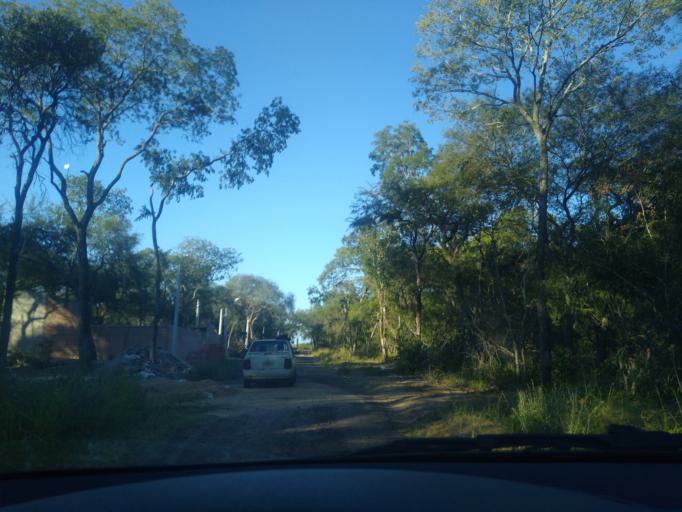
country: AR
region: Chaco
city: Resistencia
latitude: -27.4111
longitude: -58.9534
